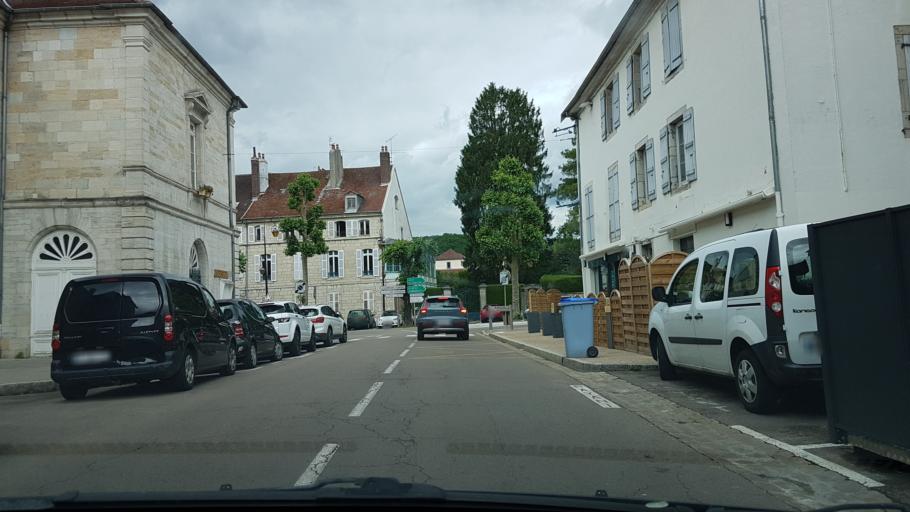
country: FR
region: Franche-Comte
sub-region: Departement du Jura
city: Lons-le-Saunier
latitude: 46.6758
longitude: 5.5538
